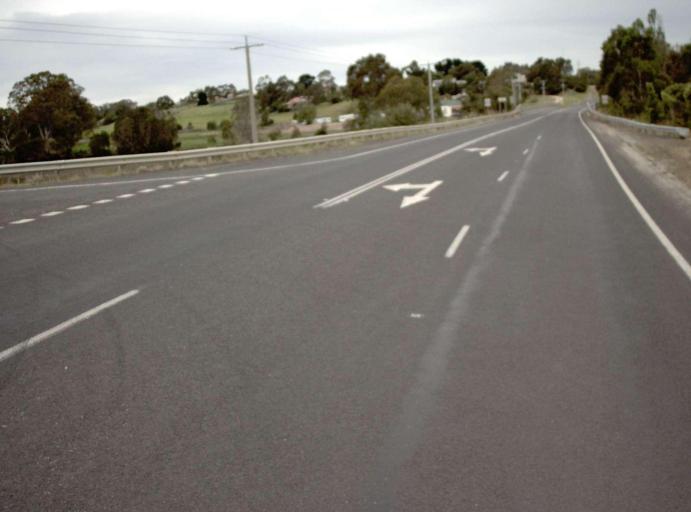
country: AU
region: Victoria
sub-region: Wellington
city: Sale
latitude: -38.1535
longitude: 147.0829
